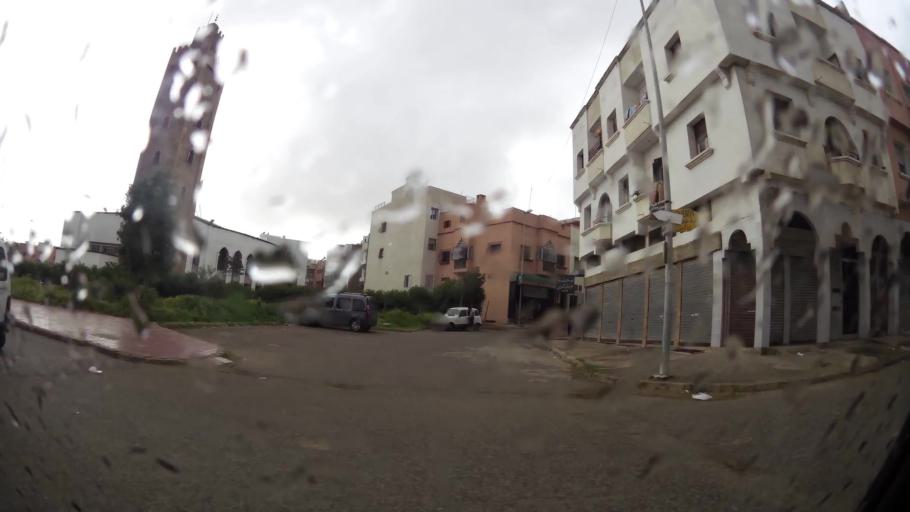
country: MA
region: Grand Casablanca
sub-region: Casablanca
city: Casablanca
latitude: 33.5642
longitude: -7.6906
